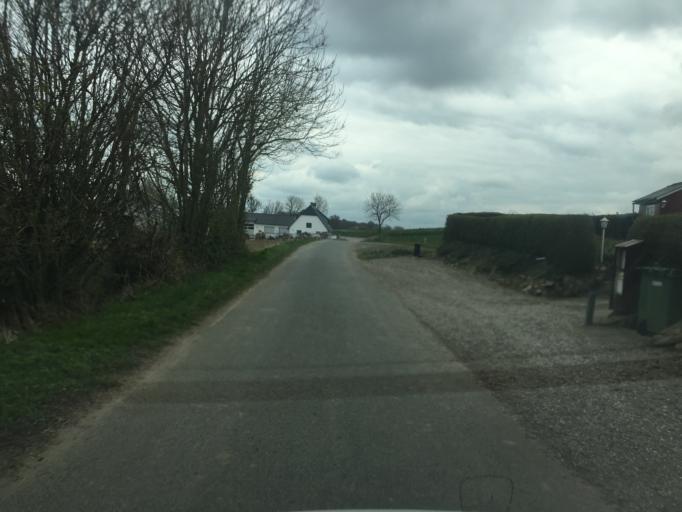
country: DK
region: South Denmark
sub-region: Sonderborg Kommune
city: Grasten
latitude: 55.0051
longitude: 9.5389
